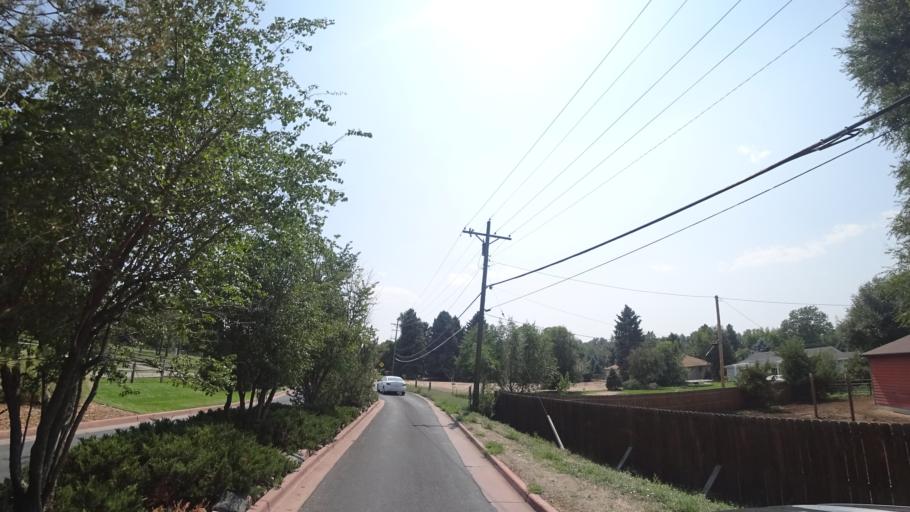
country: US
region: Colorado
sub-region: Arapahoe County
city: Greenwood Village
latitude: 39.6147
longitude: -104.9787
